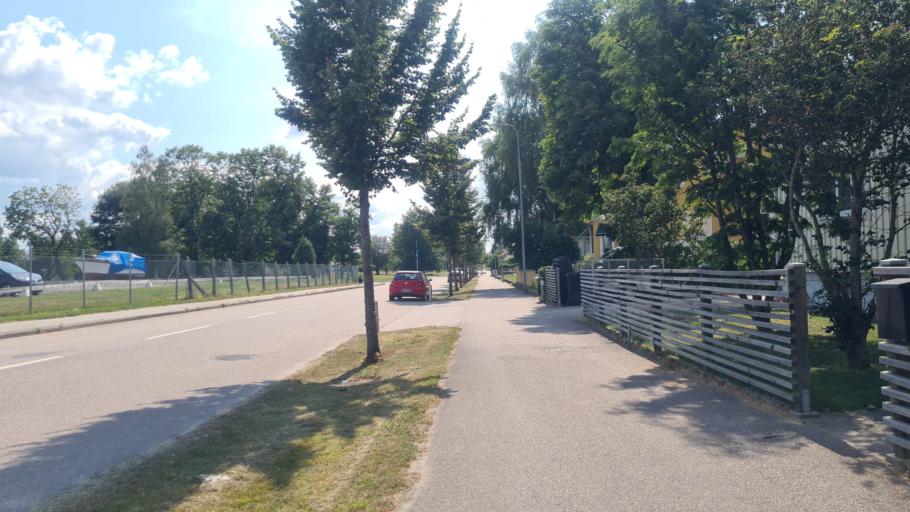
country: SE
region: Kronoberg
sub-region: Ljungby Kommun
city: Ljungby
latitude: 56.8300
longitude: 13.9283
